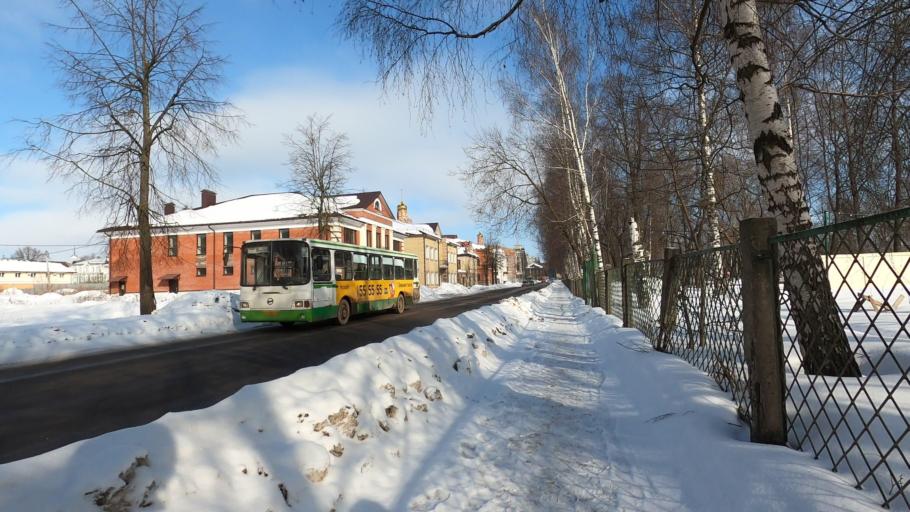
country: RU
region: Jaroslavl
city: Rybinsk
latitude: 58.0438
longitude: 38.8496
